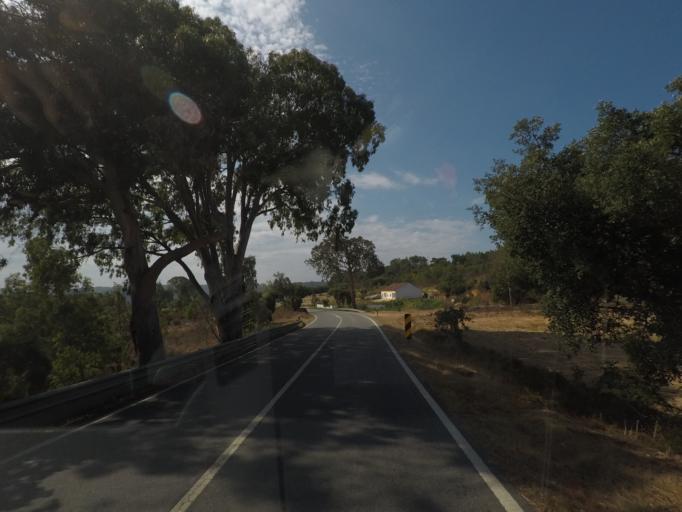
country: PT
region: Beja
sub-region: Odemira
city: Sao Teotonio
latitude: 37.4418
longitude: -8.7568
